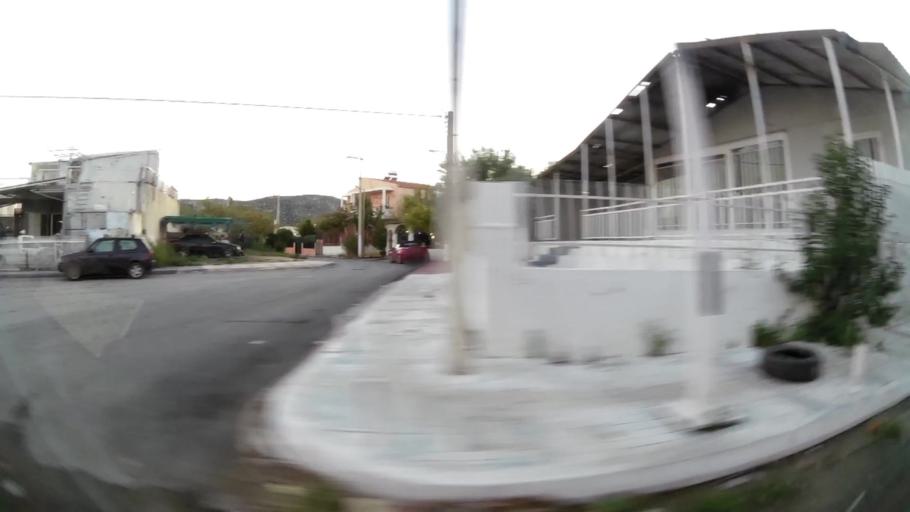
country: GR
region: Attica
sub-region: Nomarchia Dytikis Attikis
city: Ano Liosia
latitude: 38.0815
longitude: 23.6934
